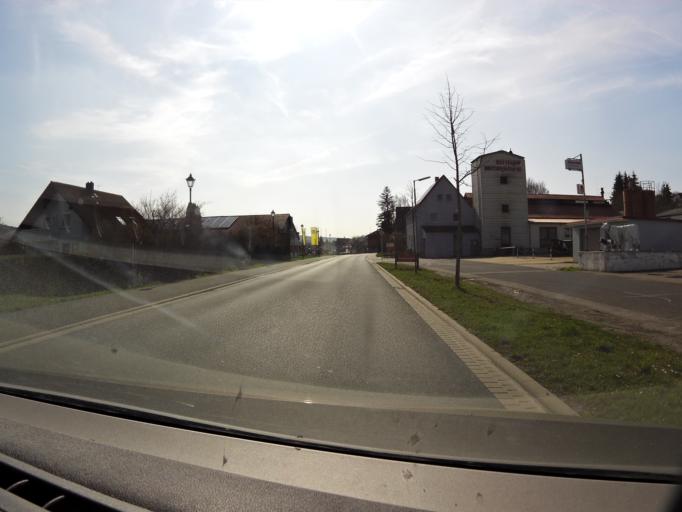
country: DE
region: Bavaria
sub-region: Regierungsbezirk Unterfranken
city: Rottingen
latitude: 49.5128
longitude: 9.9767
